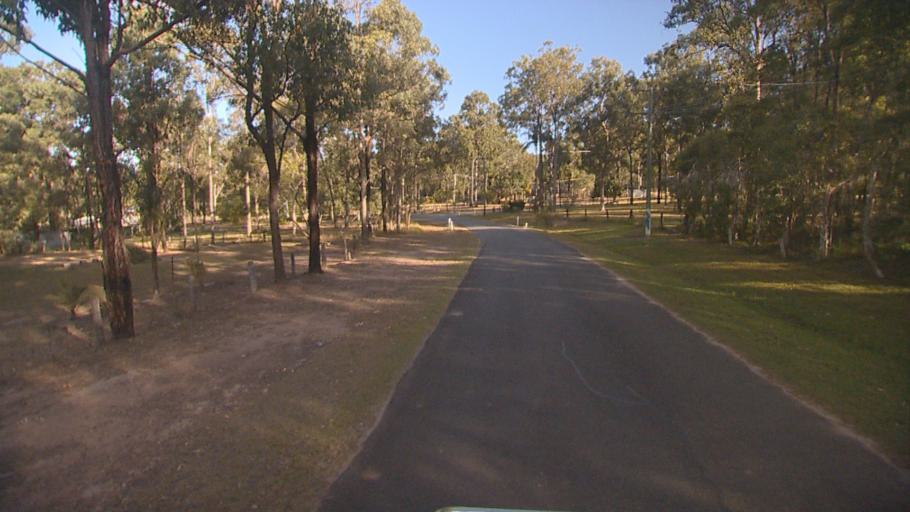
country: AU
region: Queensland
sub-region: Ipswich
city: Springfield Lakes
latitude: -27.6982
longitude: 152.9543
